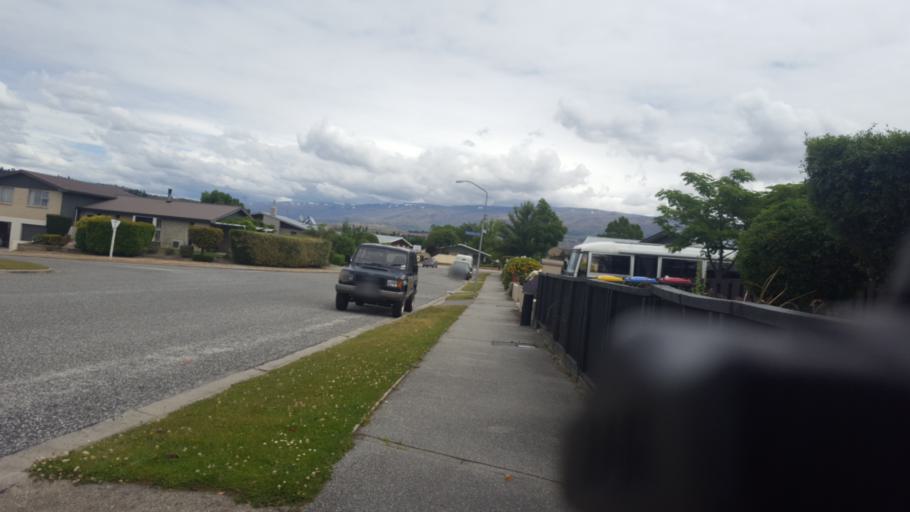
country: NZ
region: Otago
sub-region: Queenstown-Lakes District
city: Wanaka
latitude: -45.2462
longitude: 169.3811
